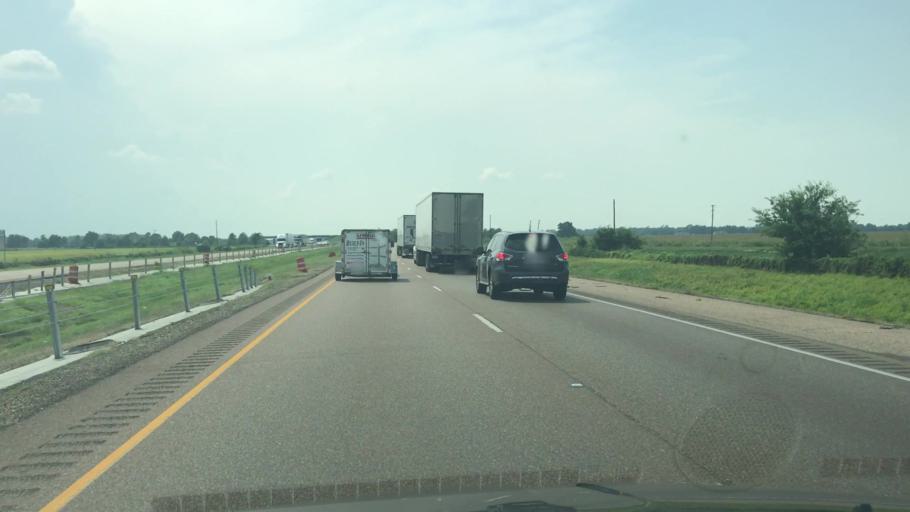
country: US
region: Arkansas
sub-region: Crittenden County
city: Earle
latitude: 35.1513
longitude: -90.3917
